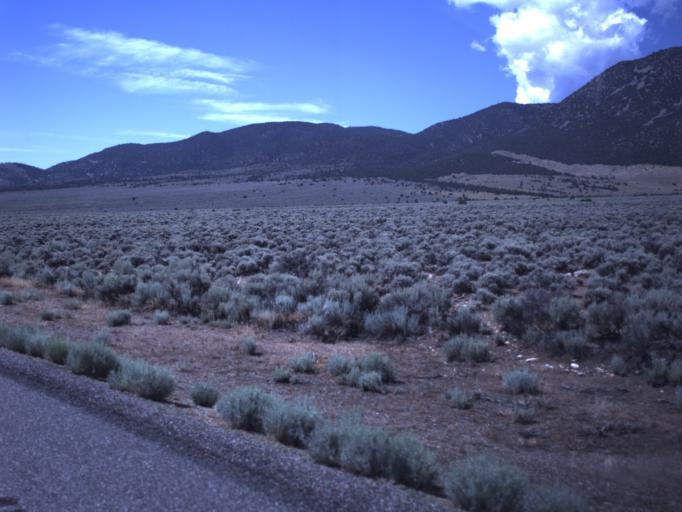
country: US
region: Utah
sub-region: Piute County
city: Junction
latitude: 38.3753
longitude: -112.2267
